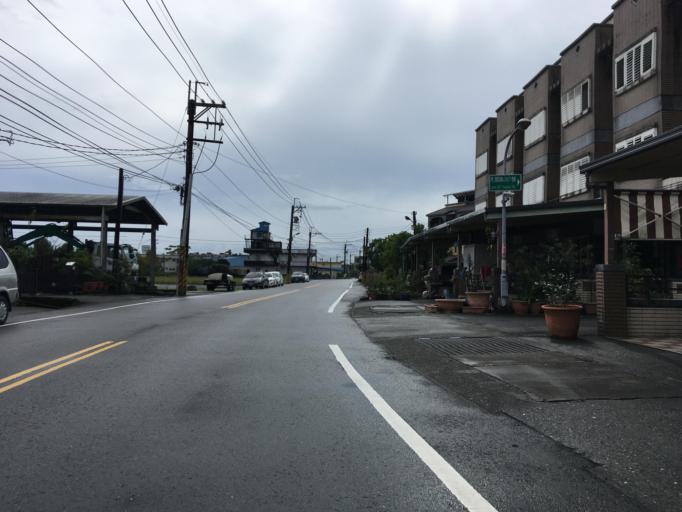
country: TW
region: Taiwan
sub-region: Yilan
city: Yilan
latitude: 24.6666
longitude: 121.7928
